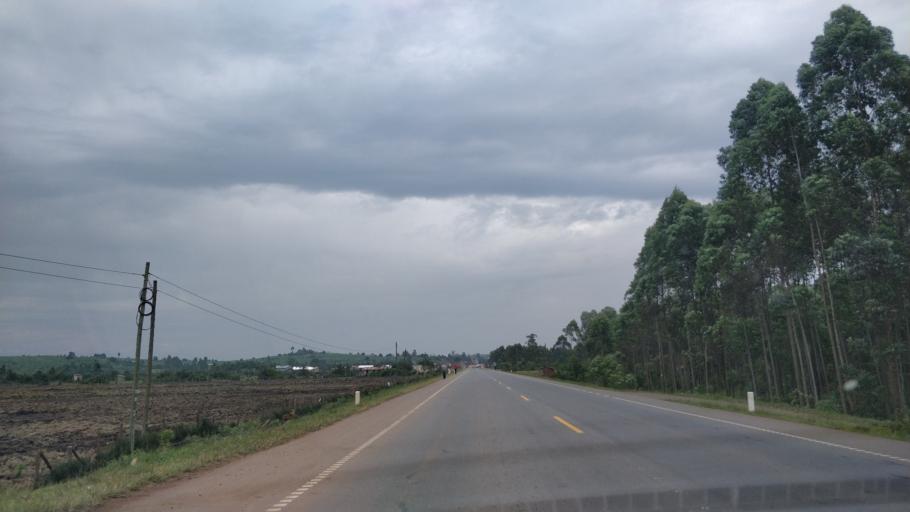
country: UG
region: Western Region
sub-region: Sheema District
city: Kibingo
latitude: -0.6659
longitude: 30.4476
